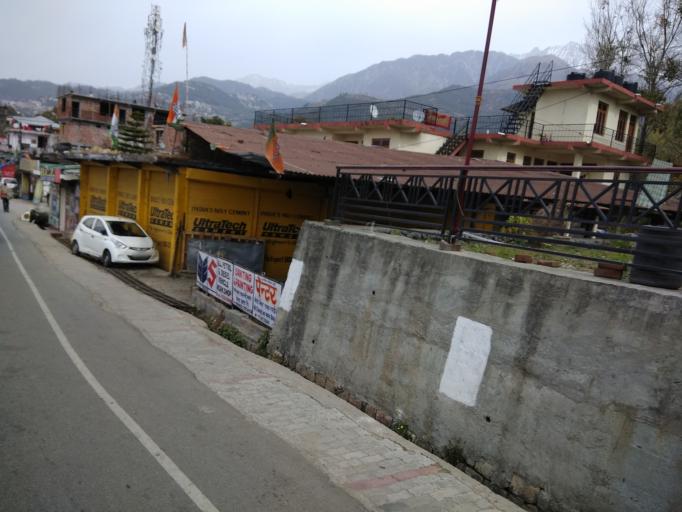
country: IN
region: Himachal Pradesh
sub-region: Kangra
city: Dharmsala
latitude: 32.1993
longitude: 76.3367
